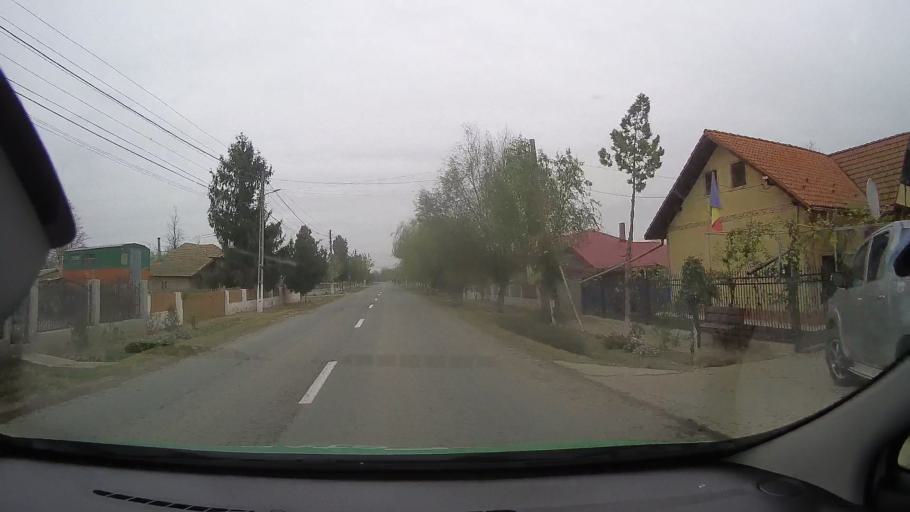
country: RO
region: Constanta
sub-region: Comuna Silistea
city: Silistea
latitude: 44.4438
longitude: 28.2354
